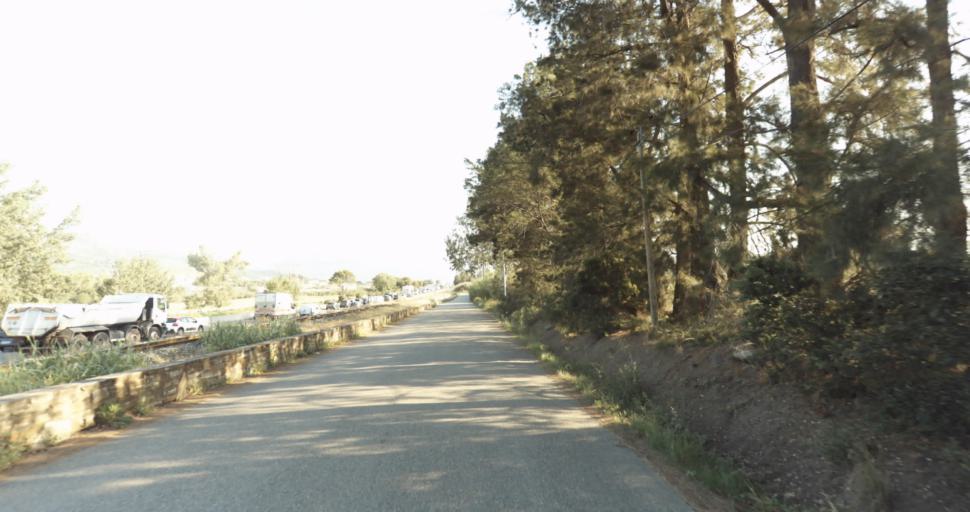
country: FR
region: Corsica
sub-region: Departement de la Haute-Corse
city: Biguglia
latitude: 42.6087
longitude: 9.4383
